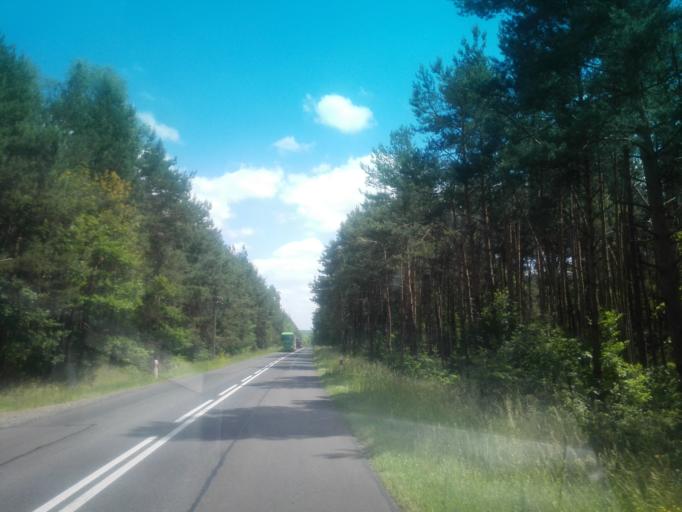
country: PL
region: Silesian Voivodeship
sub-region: Powiat czestochowski
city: Potok Zloty
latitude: 50.7393
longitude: 19.3578
